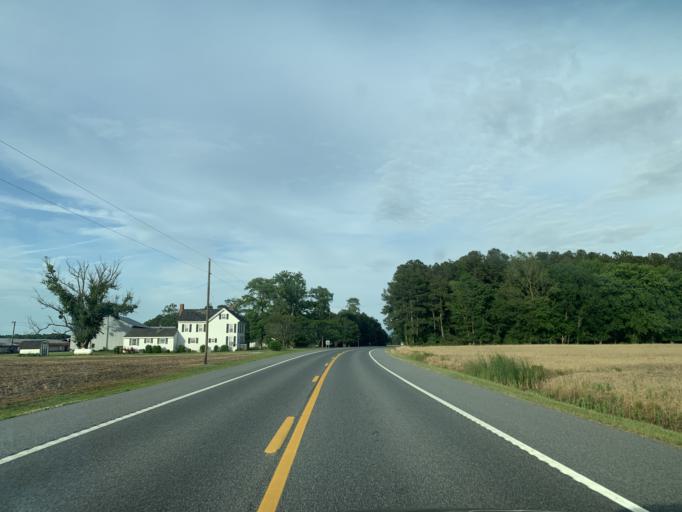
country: US
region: Virginia
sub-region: Accomack County
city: Captains Cove
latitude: 38.0697
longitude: -75.4535
